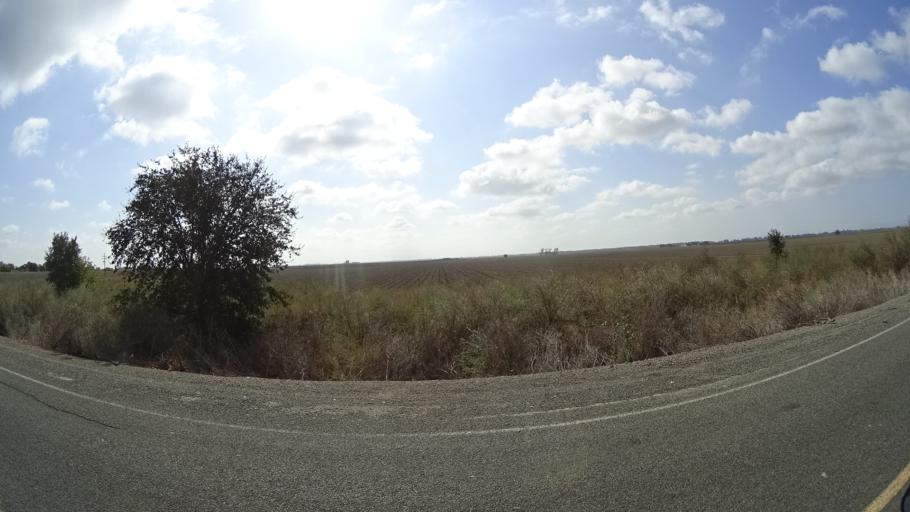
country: US
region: California
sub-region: Yolo County
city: Woodland
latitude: 38.7485
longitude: -121.6962
